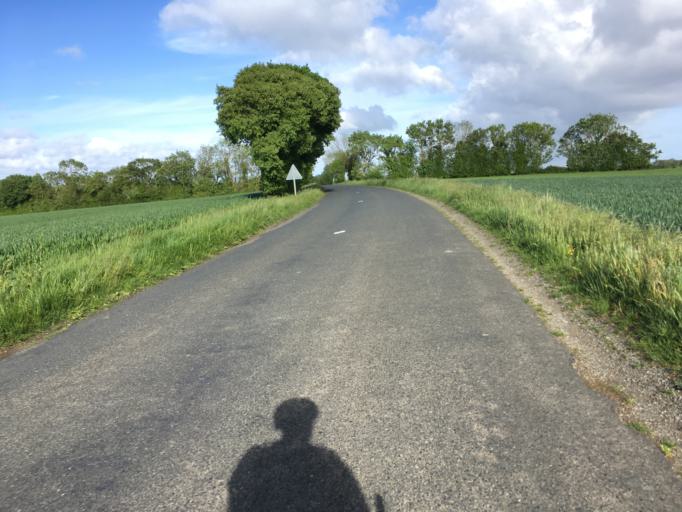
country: FR
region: Poitou-Charentes
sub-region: Departement de la Charente-Maritime
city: Verines
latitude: 46.1691
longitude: -0.8833
